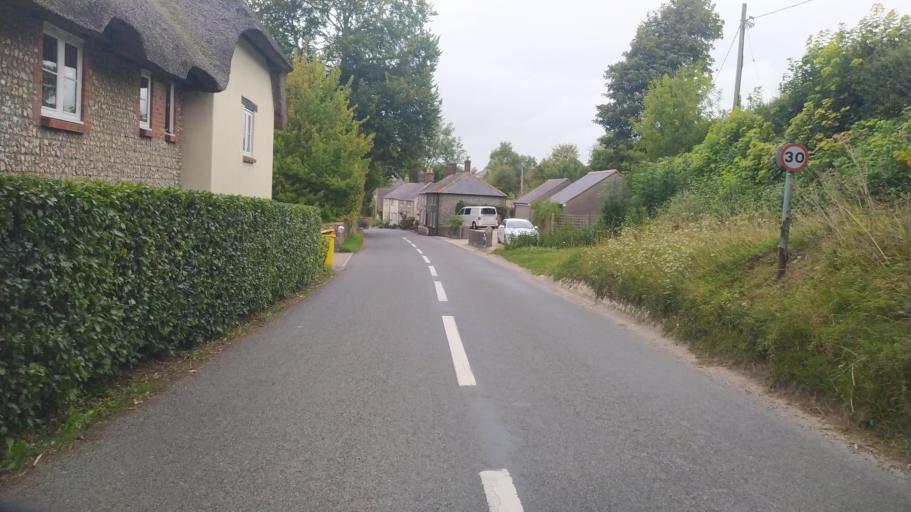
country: GB
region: England
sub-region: Dorset
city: Dorchester
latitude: 50.7730
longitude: -2.4037
